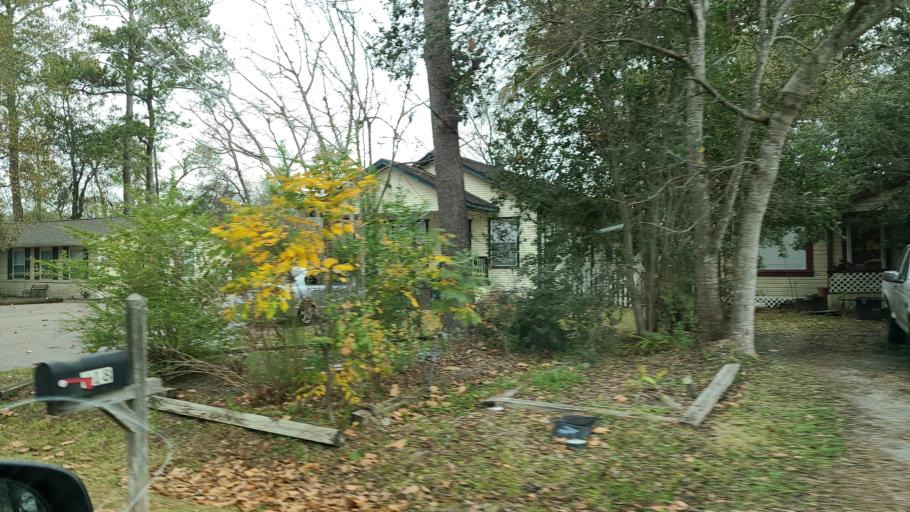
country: US
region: Texas
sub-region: Harris County
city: Spring
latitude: 30.0800
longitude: -95.4205
